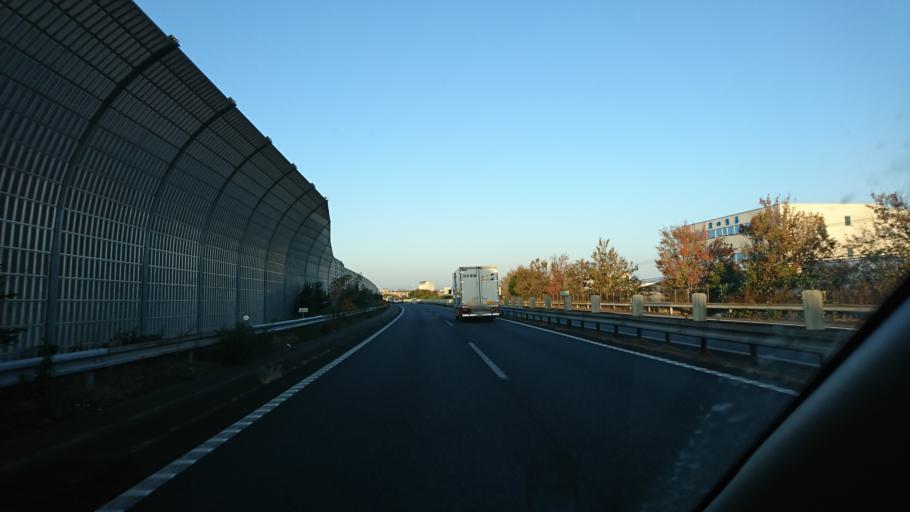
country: JP
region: Hyogo
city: Akashi
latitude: 34.7150
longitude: 134.9330
